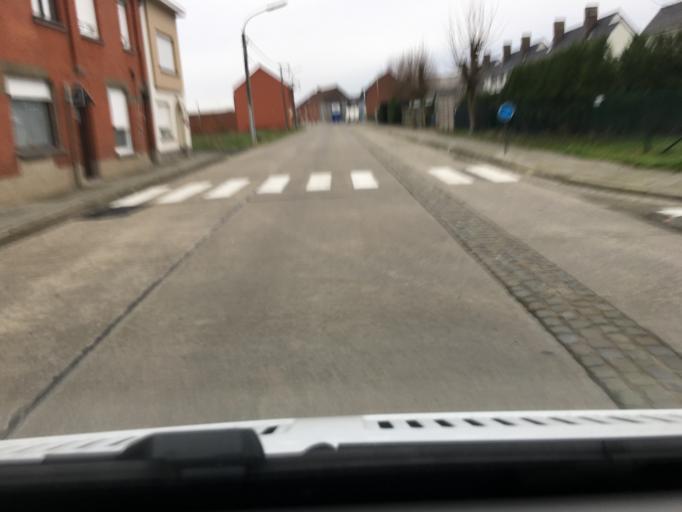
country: FR
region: Nord-Pas-de-Calais
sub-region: Departement du Nord
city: Bousbecque
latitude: 50.7808
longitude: 3.0679
